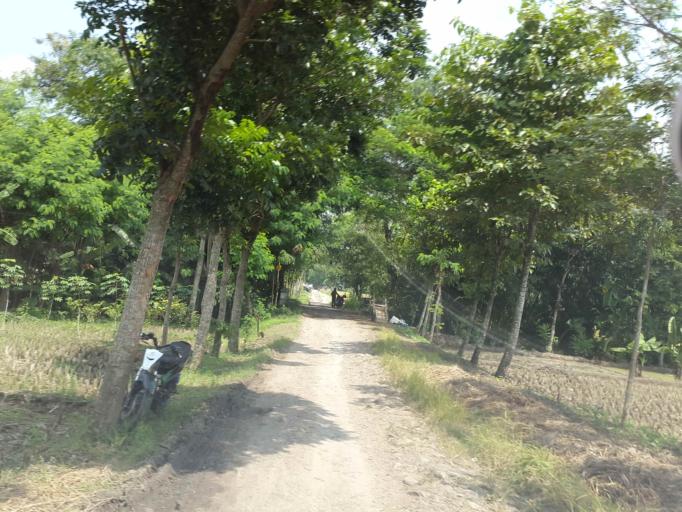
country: ID
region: Central Java
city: Dukuhkopi
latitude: -6.9630
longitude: 108.8341
